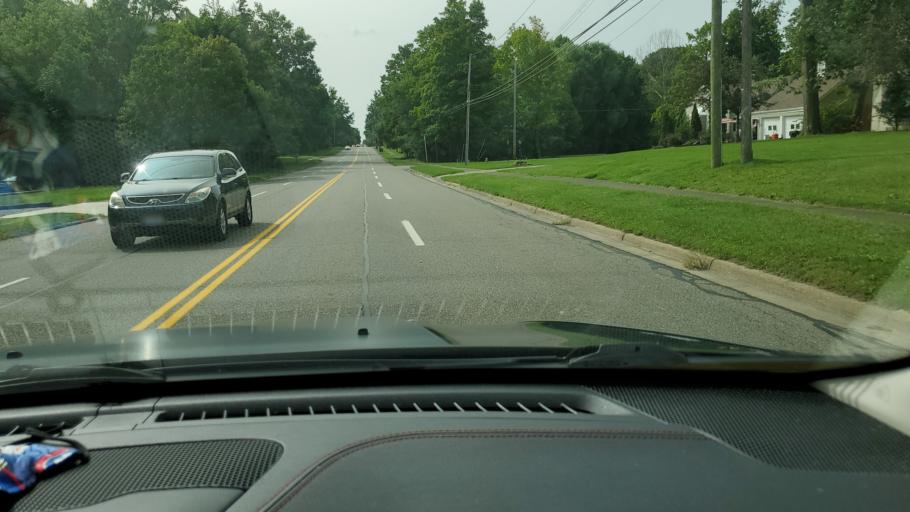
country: US
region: Ohio
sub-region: Mahoning County
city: Boardman
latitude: 41.0446
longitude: -80.6723
